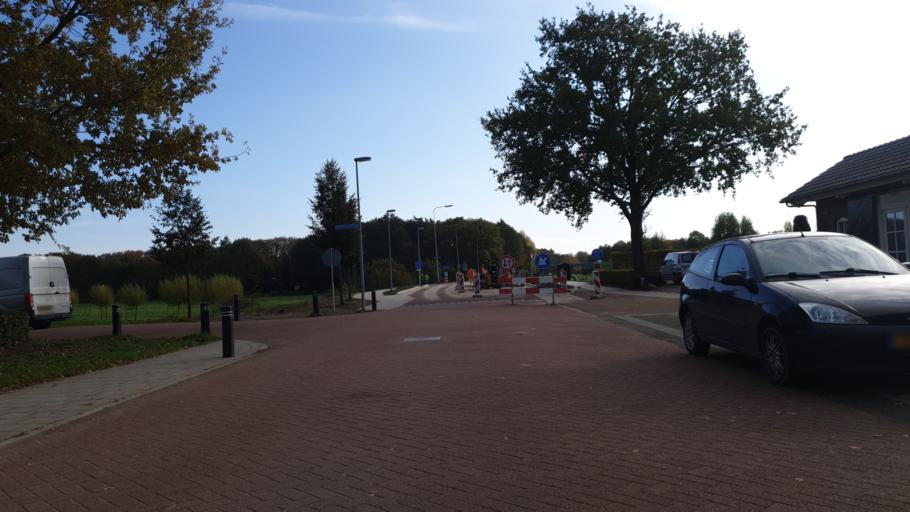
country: NL
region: Limburg
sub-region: Gemeente Gennep
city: Gennep
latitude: 51.6691
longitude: 5.9808
